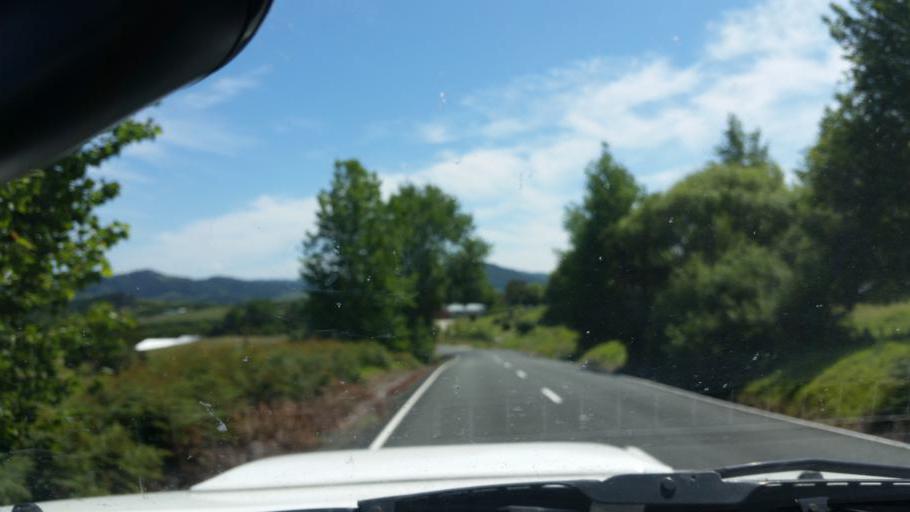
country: NZ
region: Auckland
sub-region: Auckland
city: Wellsford
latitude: -36.1819
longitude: 174.4120
